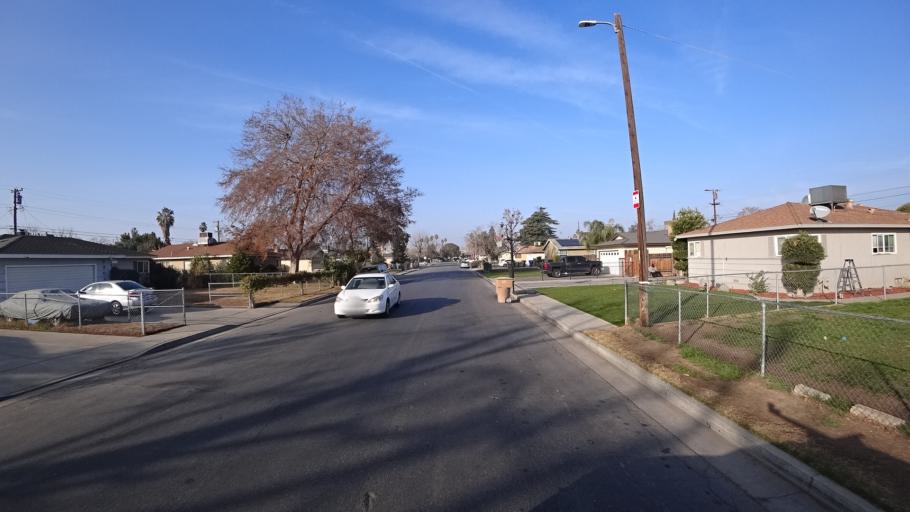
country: US
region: California
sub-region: Kern County
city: Bakersfield
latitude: 35.3370
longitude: -119.0269
